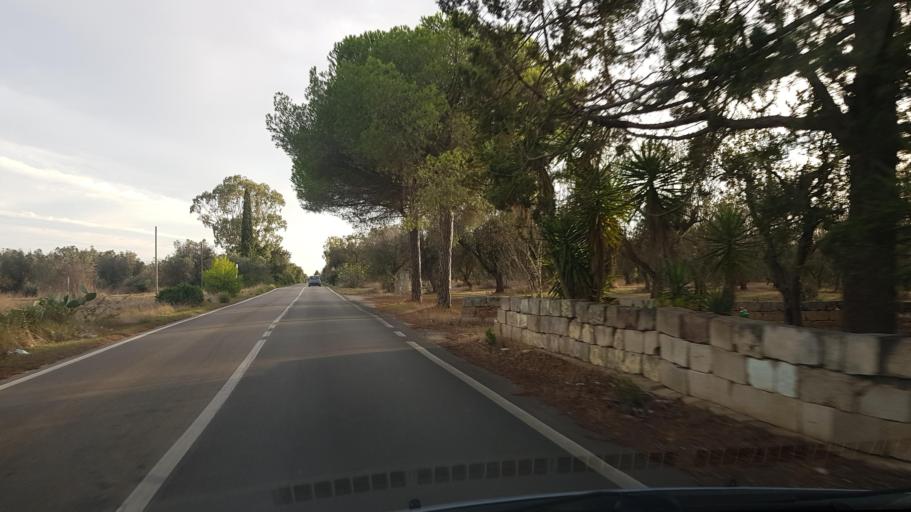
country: IT
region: Apulia
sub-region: Provincia di Brindisi
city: Torchiarolo
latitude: 40.4805
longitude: 18.1253
